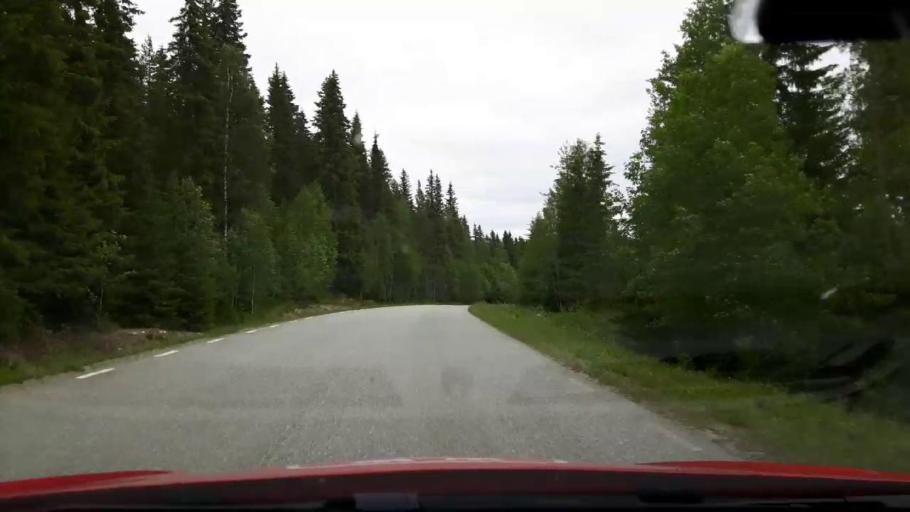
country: SE
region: Jaemtland
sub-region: Ragunda Kommun
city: Hammarstrand
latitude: 63.2142
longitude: 15.9759
